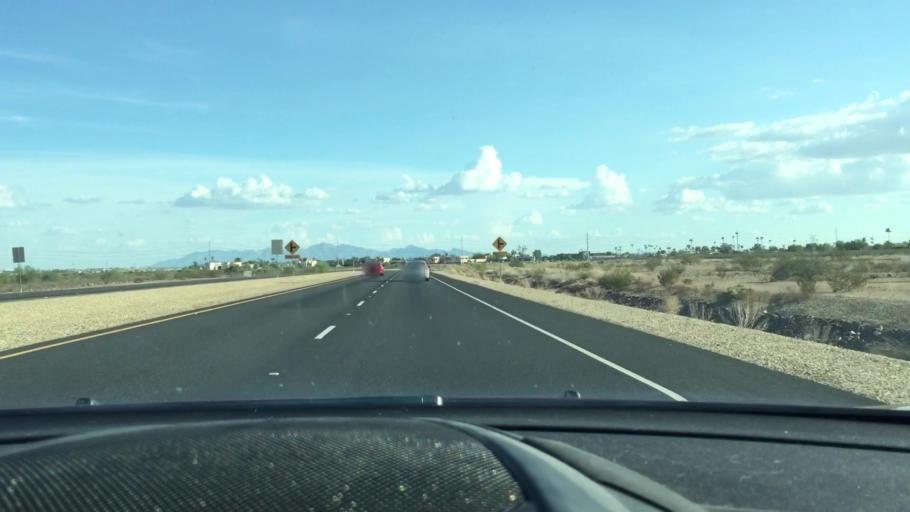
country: US
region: Arizona
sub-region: Maricopa County
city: Surprise
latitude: 33.6483
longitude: -112.3229
